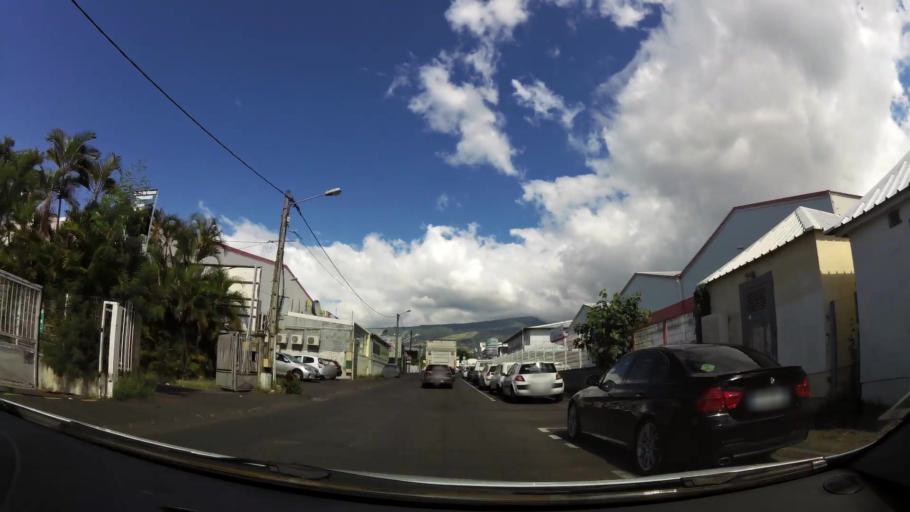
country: RE
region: Reunion
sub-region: Reunion
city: Saint-Denis
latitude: -20.8910
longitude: 55.4966
